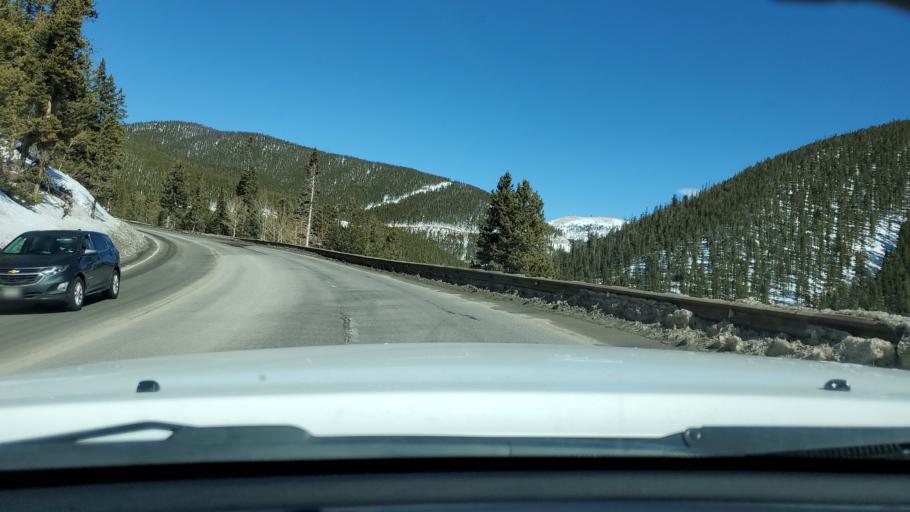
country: US
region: Colorado
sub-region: Chaffee County
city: Salida
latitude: 38.4548
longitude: -106.3425
